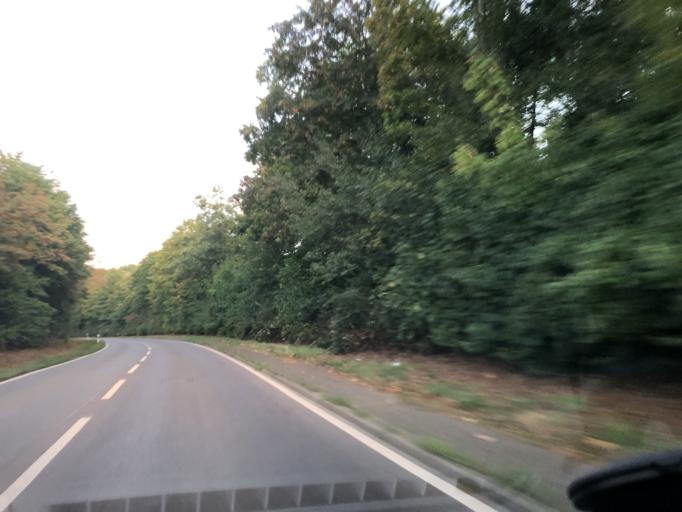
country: DE
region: Baden-Wuerttemberg
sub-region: Regierungsbezirk Stuttgart
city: Erdmannhausen
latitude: 48.8881
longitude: 9.2841
